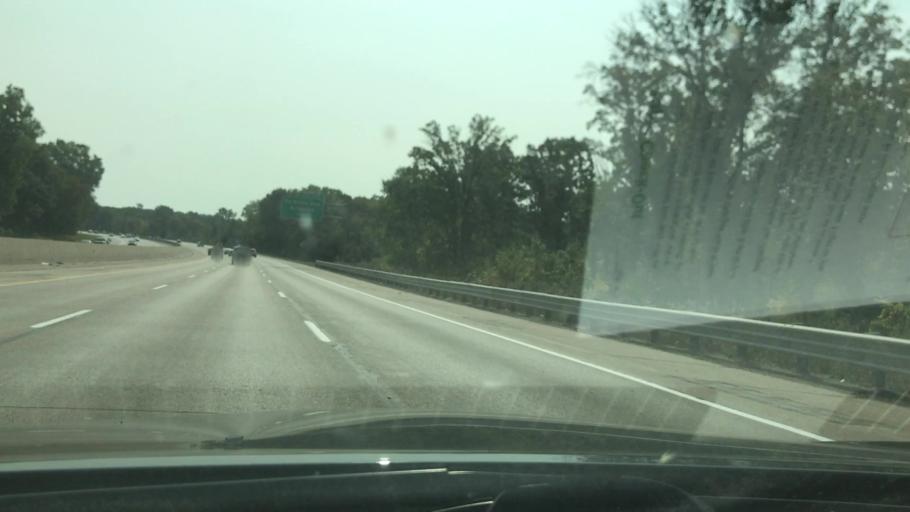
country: US
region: Michigan
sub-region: Livingston County
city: Brighton
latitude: 42.5548
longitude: -83.8180
